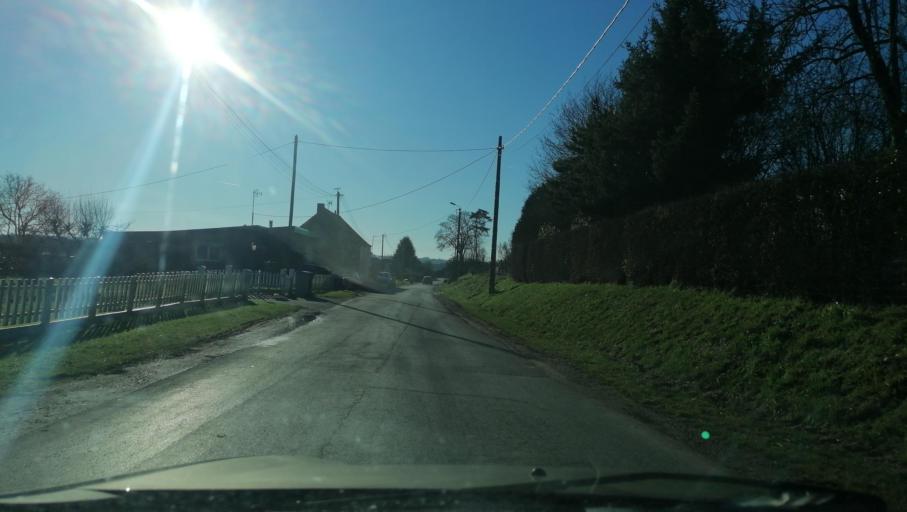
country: FR
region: Nord-Pas-de-Calais
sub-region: Departement du Nord
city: Ferriere-la-Grande
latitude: 50.2247
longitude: 4.0361
